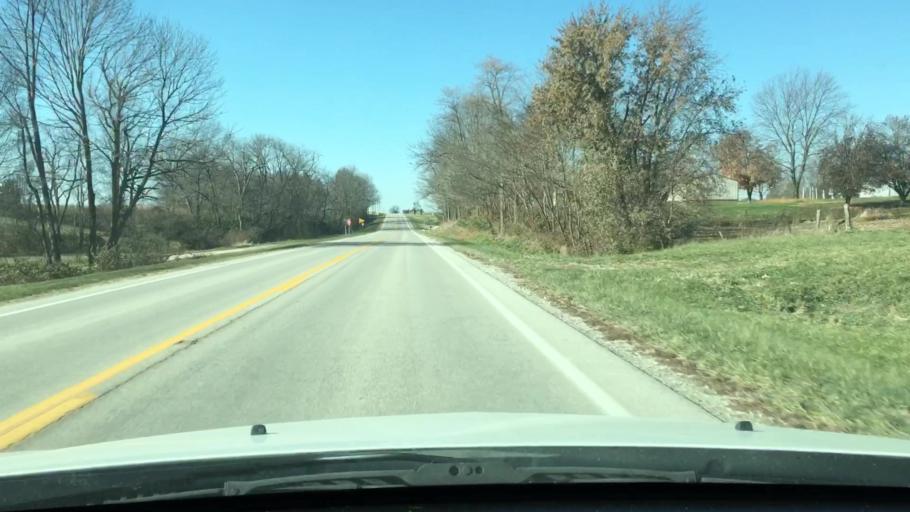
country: US
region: Illinois
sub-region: Pike County
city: Griggsville
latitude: 39.6193
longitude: -90.7083
